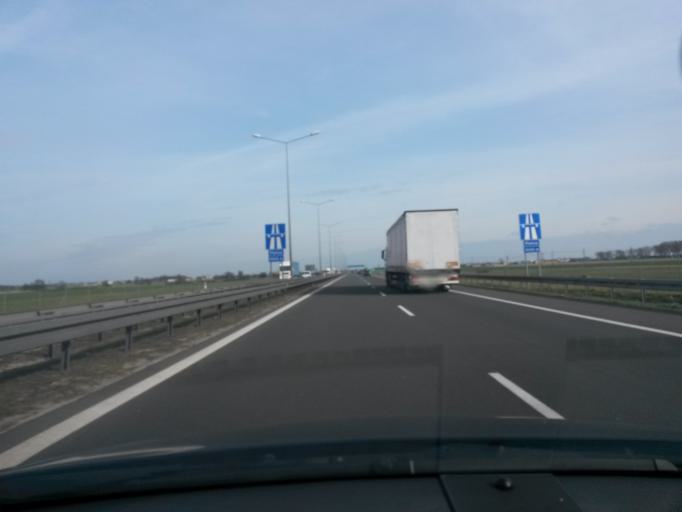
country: PL
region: Greater Poland Voivodeship
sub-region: Powiat poznanski
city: Kleszczewo
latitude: 52.3229
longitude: 17.1114
